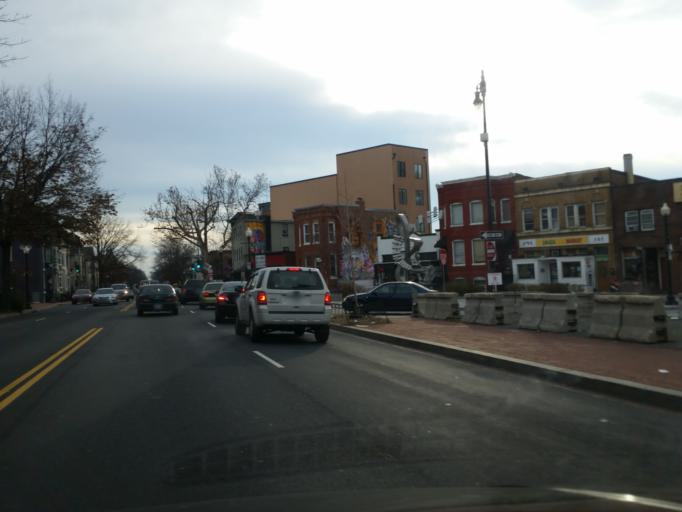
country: US
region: Washington, D.C.
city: Washington, D.C.
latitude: 38.9159
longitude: -77.0210
